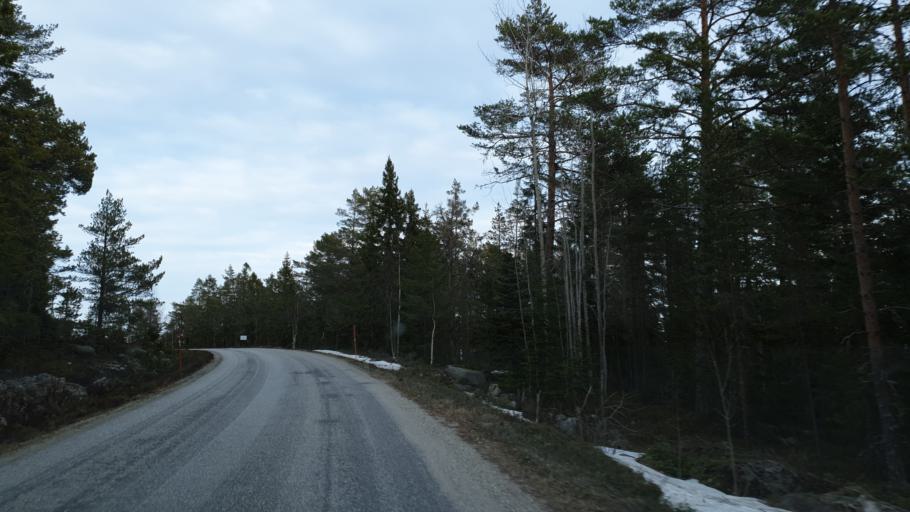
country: SE
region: Vaesternorrland
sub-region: Sundsvalls Kommun
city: Njurundabommen
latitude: 61.9669
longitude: 17.3782
